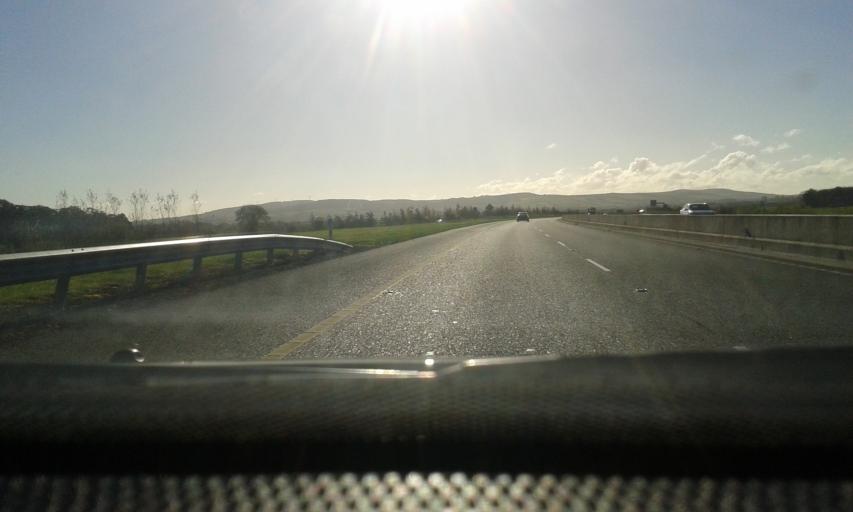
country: IE
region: Leinster
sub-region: Laois
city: Rathdowney
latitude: 52.8662
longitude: -7.4846
